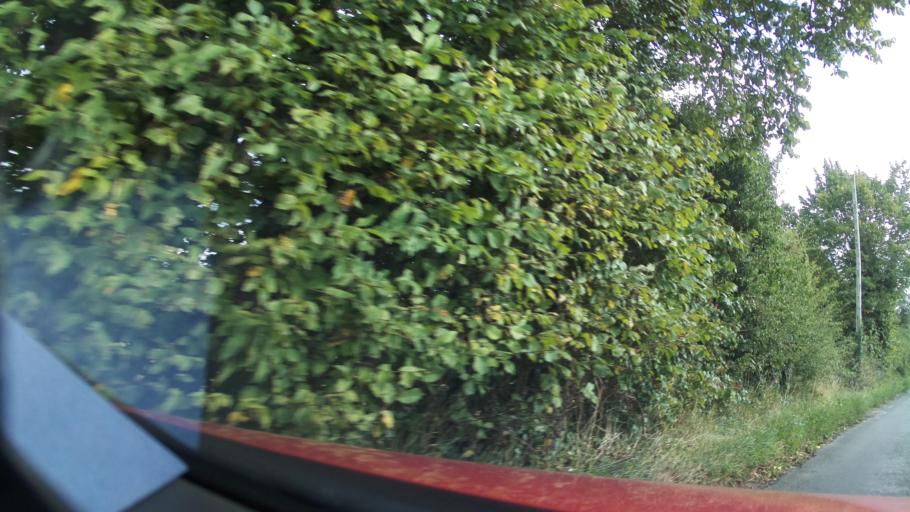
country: GB
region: England
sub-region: North Yorkshire
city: Leyburn
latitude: 54.2609
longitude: -1.7258
